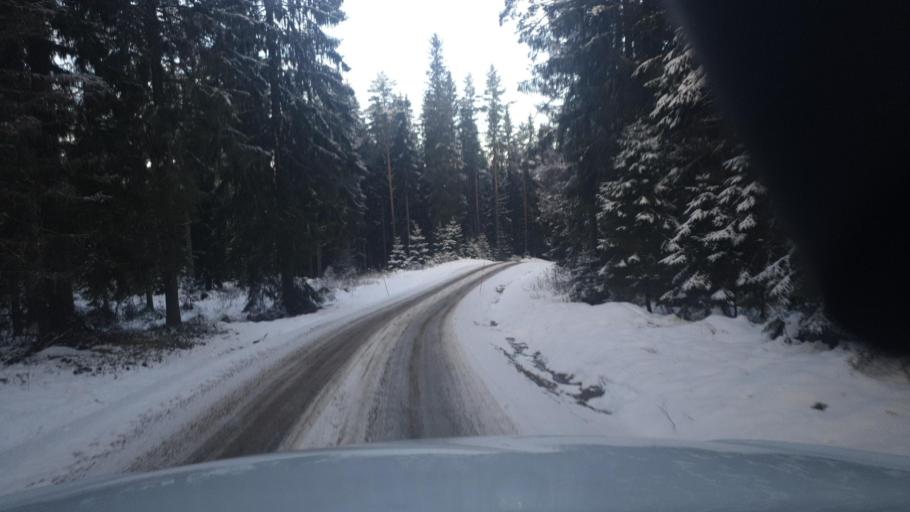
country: SE
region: Vaermland
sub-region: Arvika Kommun
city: Arvika
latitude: 59.9803
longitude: 12.6608
